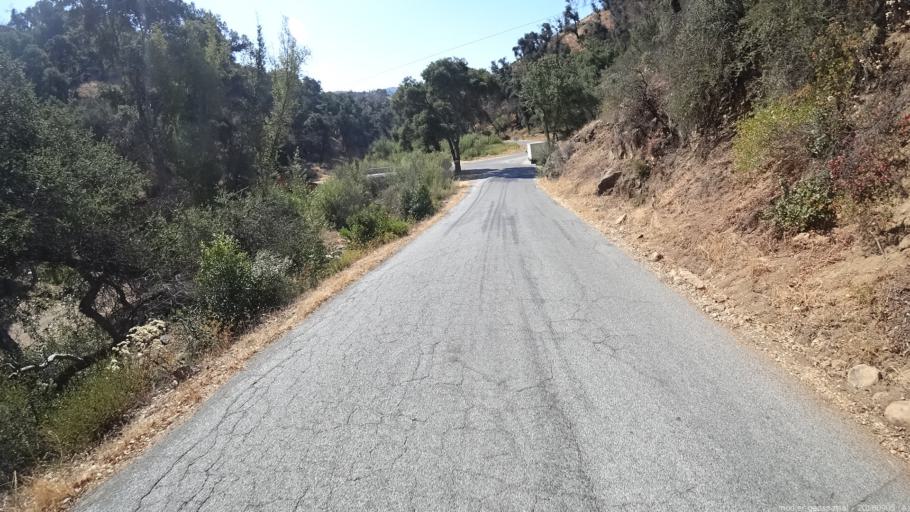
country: US
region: California
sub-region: Monterey County
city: Gonzales
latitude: 36.3915
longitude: -121.5952
